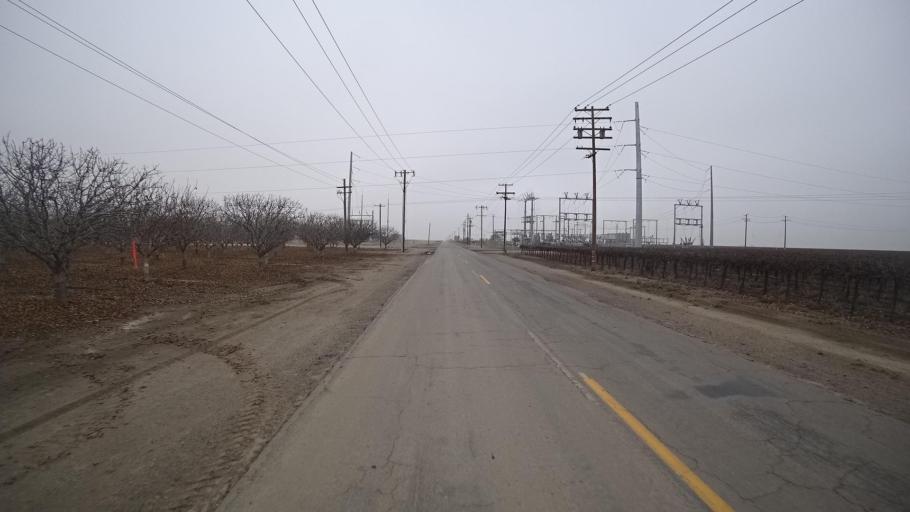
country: US
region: California
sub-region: Kern County
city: Wasco
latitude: 35.7175
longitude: -119.4541
